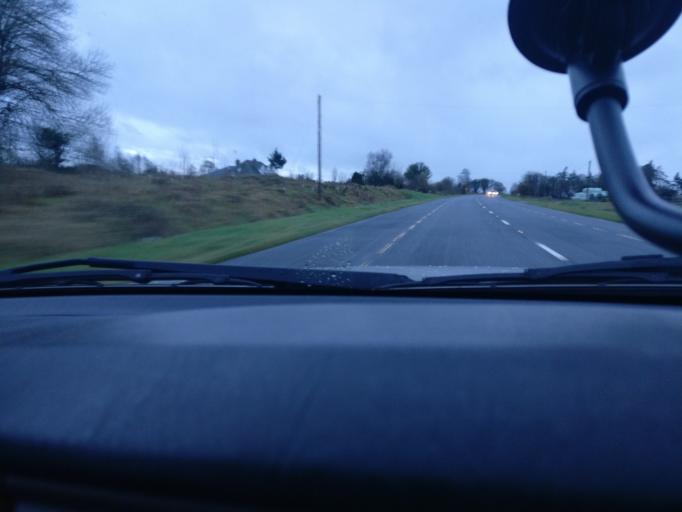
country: IE
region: Connaught
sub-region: County Galway
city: Ballinasloe
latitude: 53.2974
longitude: -8.3248
